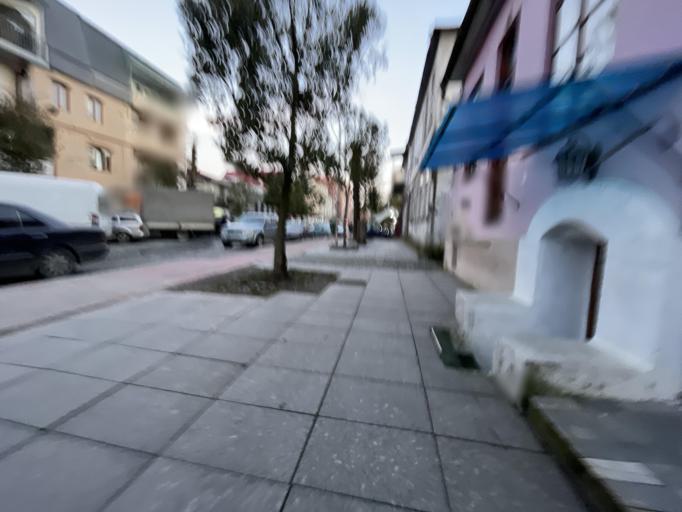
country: GE
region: Ajaria
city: Batumi
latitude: 41.6480
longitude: 41.6318
